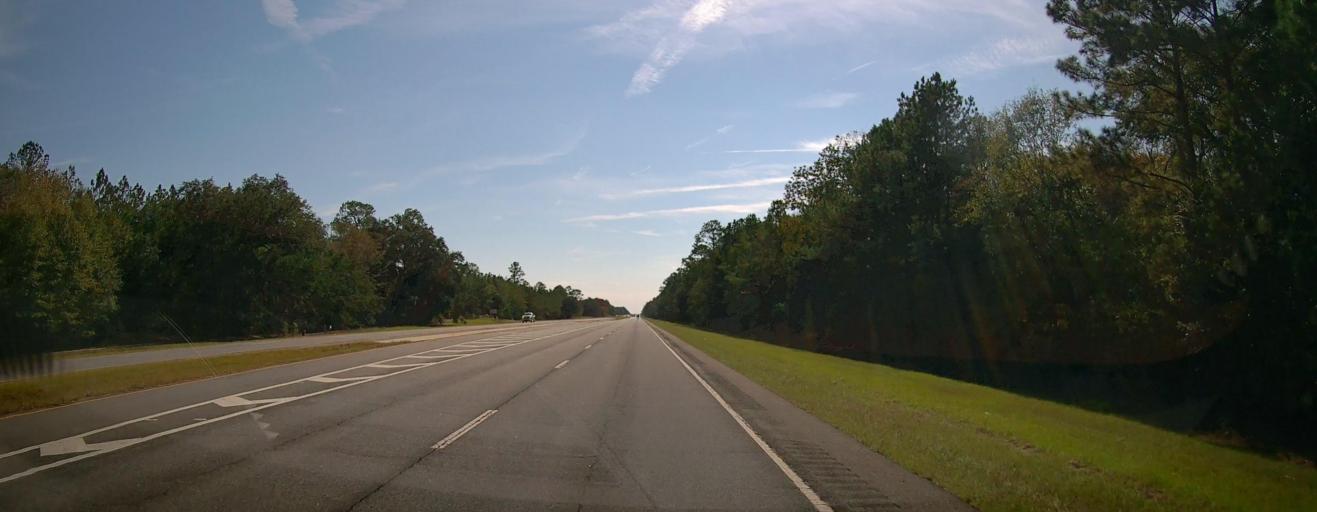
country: US
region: Georgia
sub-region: Lee County
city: Leesburg
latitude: 31.7093
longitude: -83.9901
